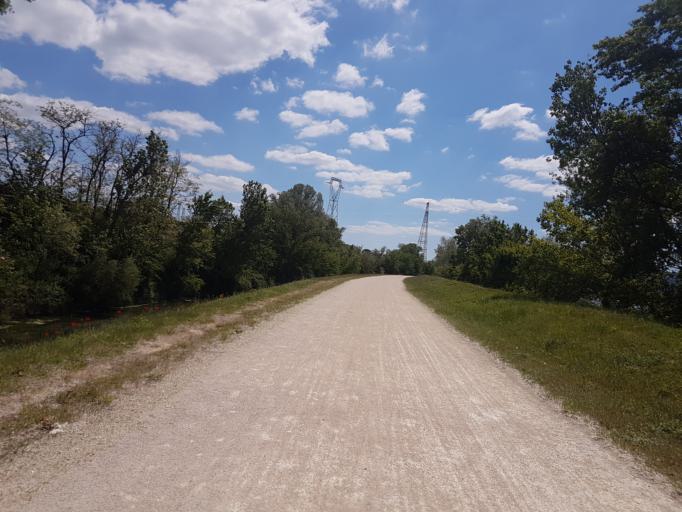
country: FR
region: Rhone-Alpes
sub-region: Departement de l'Ardeche
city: Tournon-sur-Rhone
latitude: 45.0551
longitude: 4.8623
